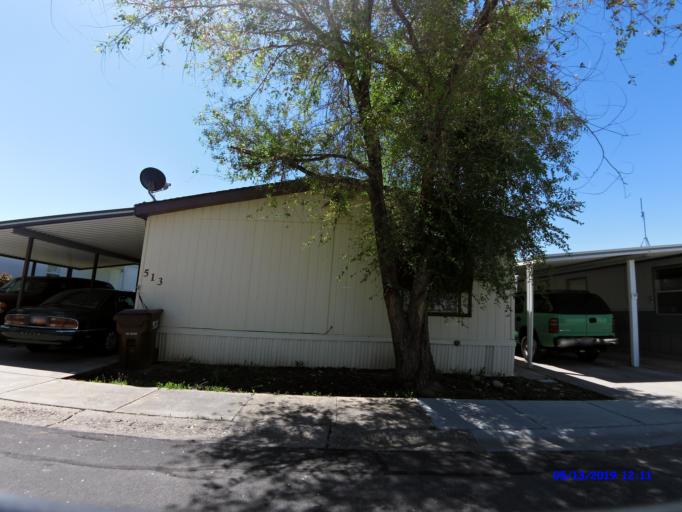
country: US
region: Utah
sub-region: Weber County
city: Harrisville
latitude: 41.2754
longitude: -111.9661
